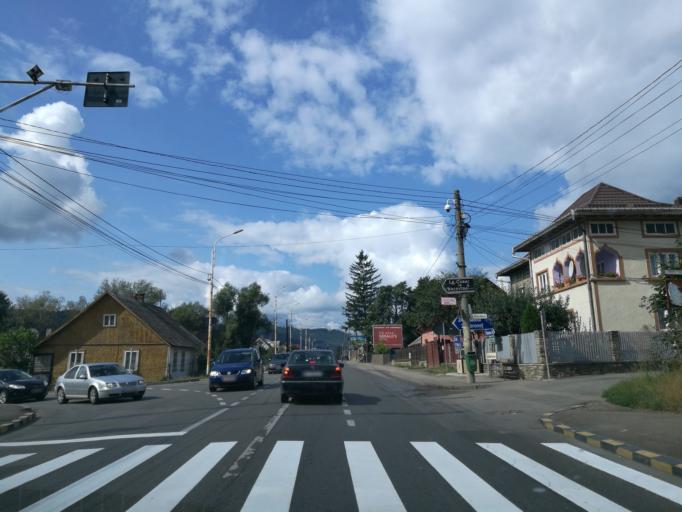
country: RO
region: Suceava
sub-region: Oras Gura Humorului
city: Gura Humorului
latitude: 47.5486
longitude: 25.8726
